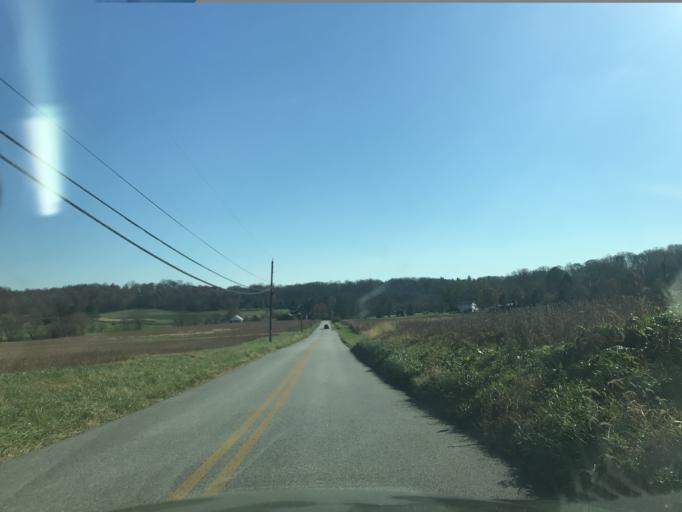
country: US
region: Maryland
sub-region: Baltimore County
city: Perry Hall
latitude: 39.4686
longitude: -76.4733
